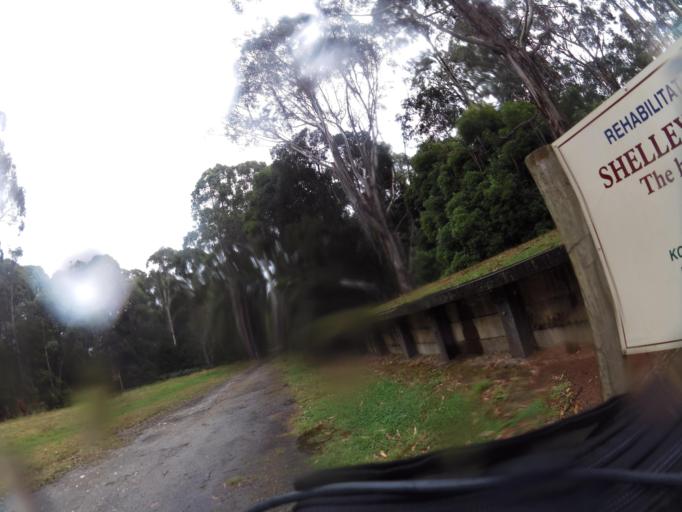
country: AU
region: New South Wales
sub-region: Greater Hume Shire
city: Holbrook
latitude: -36.1899
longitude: 147.5429
